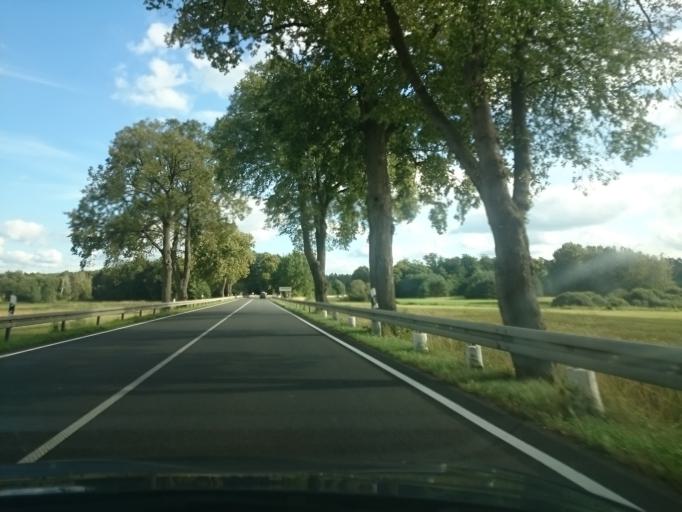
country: DE
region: Mecklenburg-Vorpommern
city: Neustrelitz
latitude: 53.3105
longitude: 13.1008
